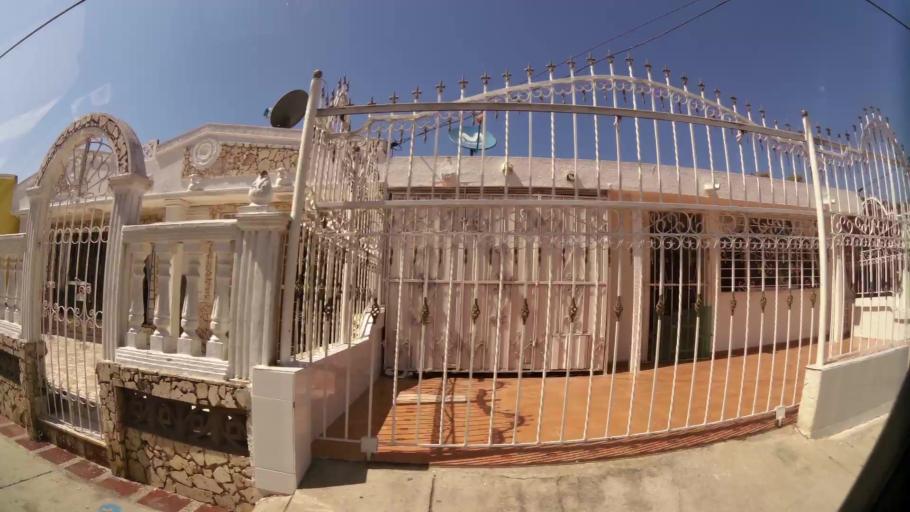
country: CO
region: Bolivar
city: Cartagena
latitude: 10.4354
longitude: -75.5260
